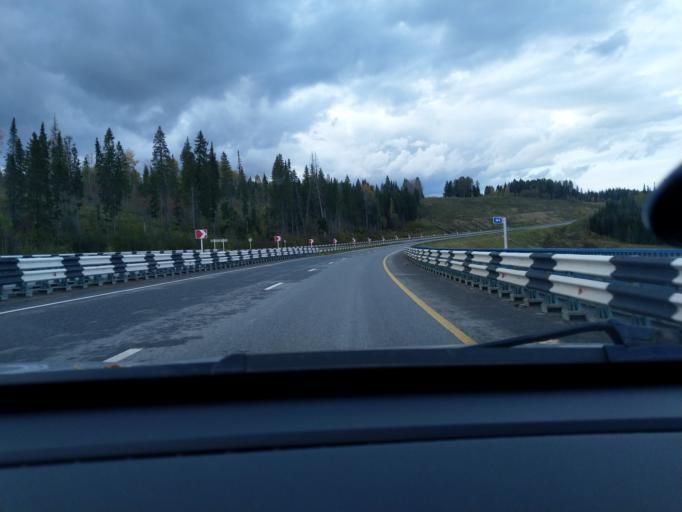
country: RU
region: Perm
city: Polazna
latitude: 58.3166
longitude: 56.4670
